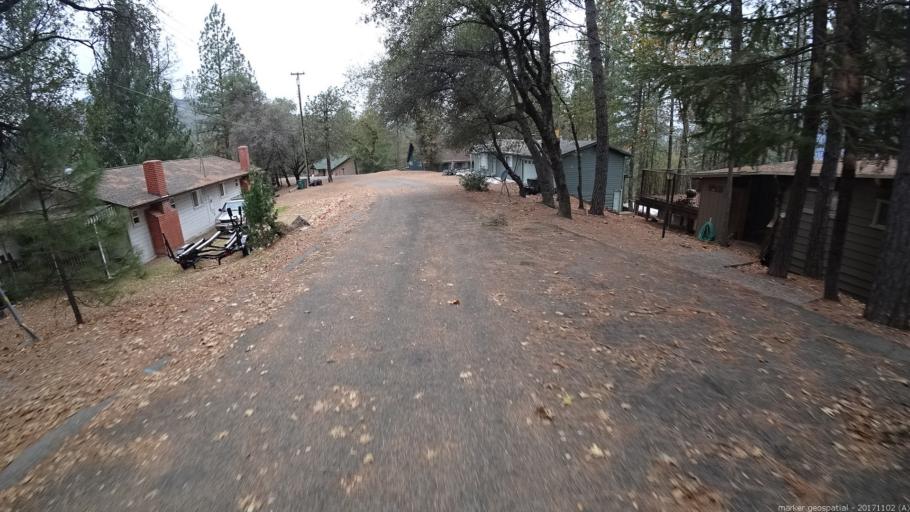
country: US
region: California
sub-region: Shasta County
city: Bella Vista
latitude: 40.7470
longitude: -122.2340
